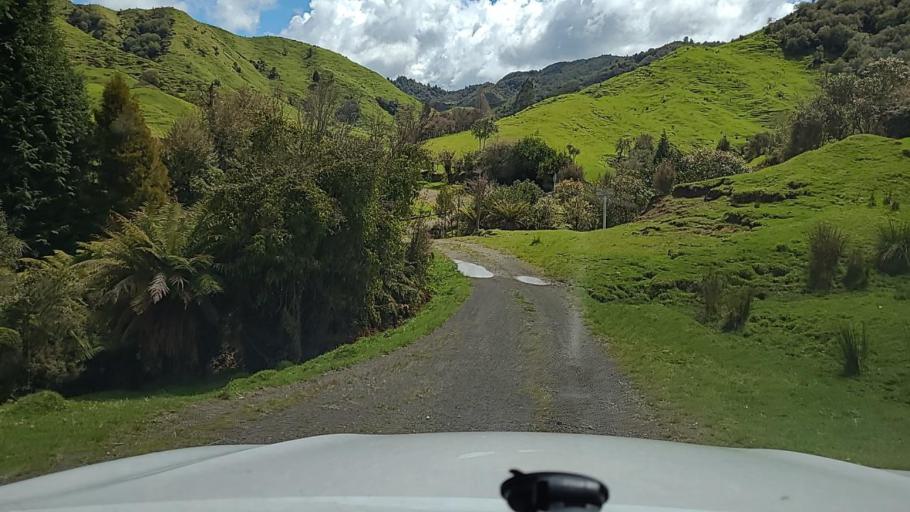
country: NZ
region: Bay of Plenty
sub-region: Opotiki District
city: Opotiki
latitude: -38.2130
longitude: 177.5905
